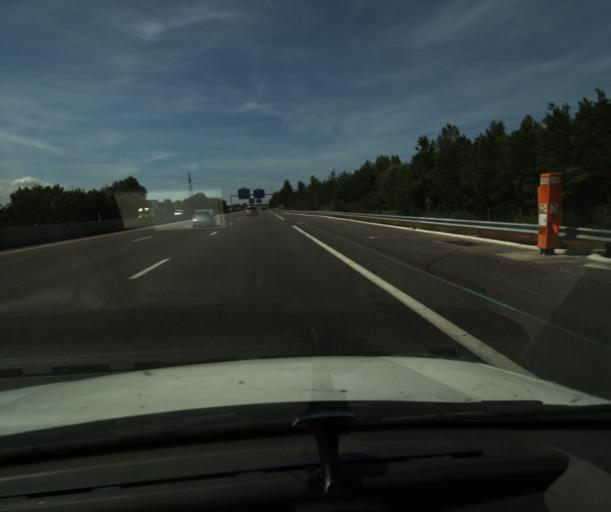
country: FR
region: Midi-Pyrenees
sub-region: Departement de la Haute-Garonne
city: Castanet-Tolosan
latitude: 43.5408
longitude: 1.5053
